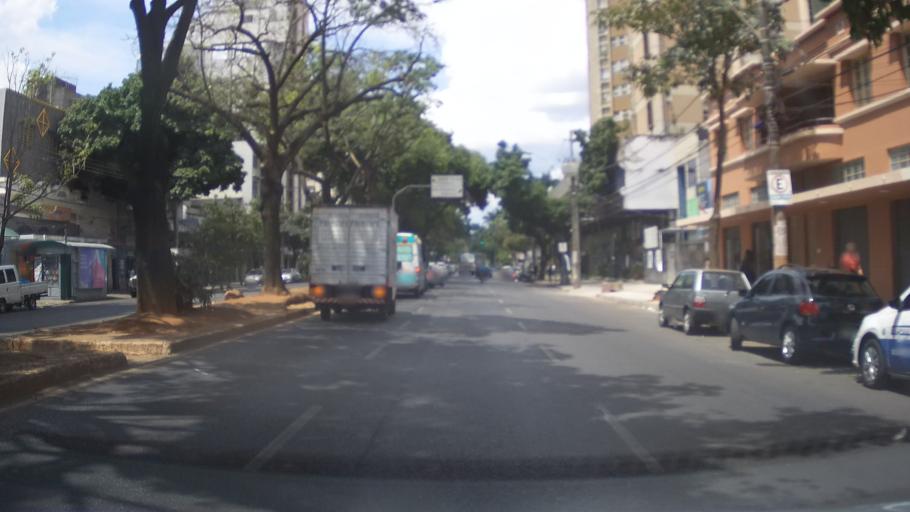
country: BR
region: Minas Gerais
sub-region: Belo Horizonte
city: Belo Horizonte
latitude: -19.9252
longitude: -43.9234
